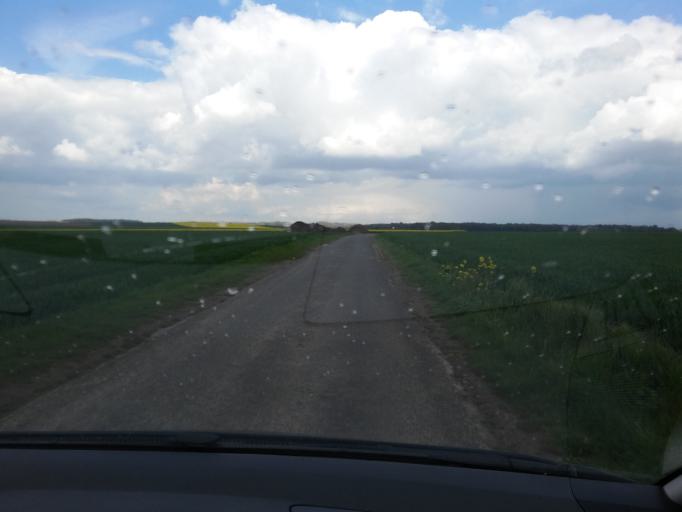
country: FR
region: Picardie
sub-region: Departement de l'Oise
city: Chevrieres
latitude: 49.3633
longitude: 2.6844
